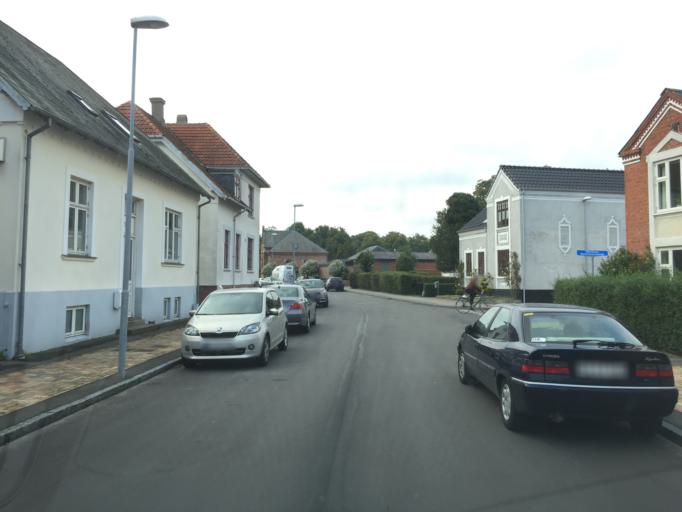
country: DK
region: South Denmark
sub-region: Nyborg Kommune
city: Nyborg
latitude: 55.3140
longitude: 10.7947
